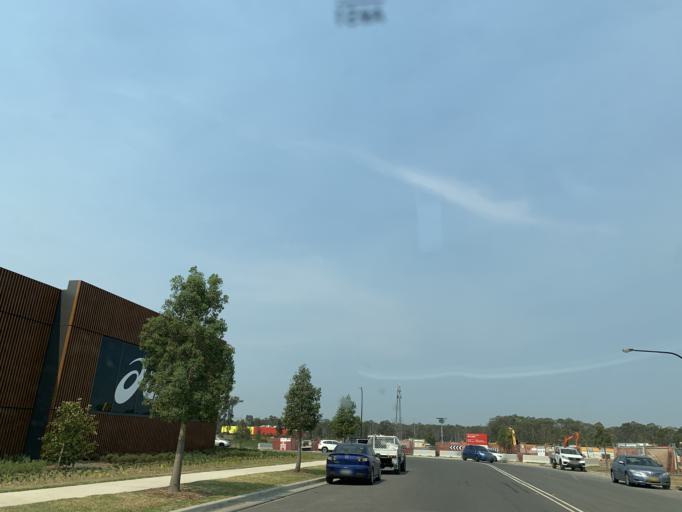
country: AU
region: New South Wales
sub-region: Blacktown
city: Hassall Grove
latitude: -33.7154
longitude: 150.8402
